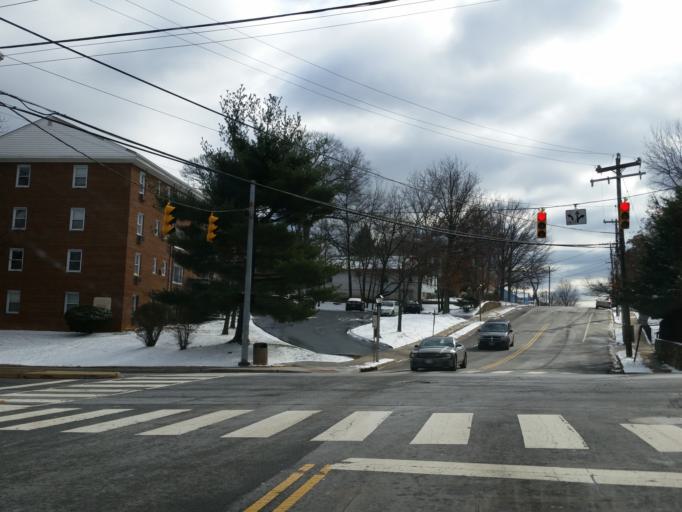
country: US
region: Virginia
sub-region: Arlington County
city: Arlington
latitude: 38.8848
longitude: -77.0879
